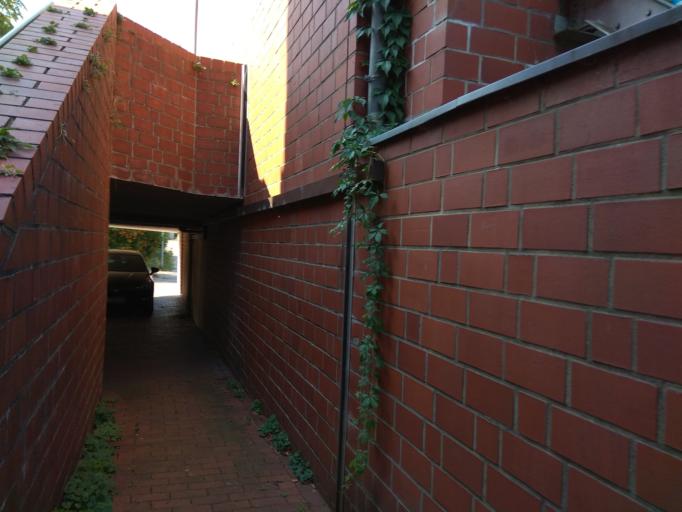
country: DE
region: North Rhine-Westphalia
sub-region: Regierungsbezirk Munster
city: Klein Reken
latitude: 51.7267
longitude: 7.0234
